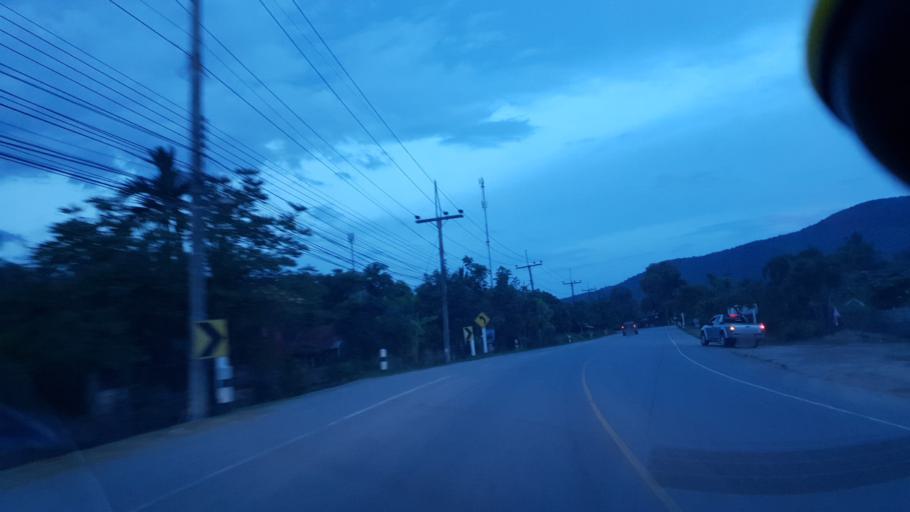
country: TH
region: Chiang Rai
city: Wiang Chiang Rung
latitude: 19.9651
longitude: 100.0075
